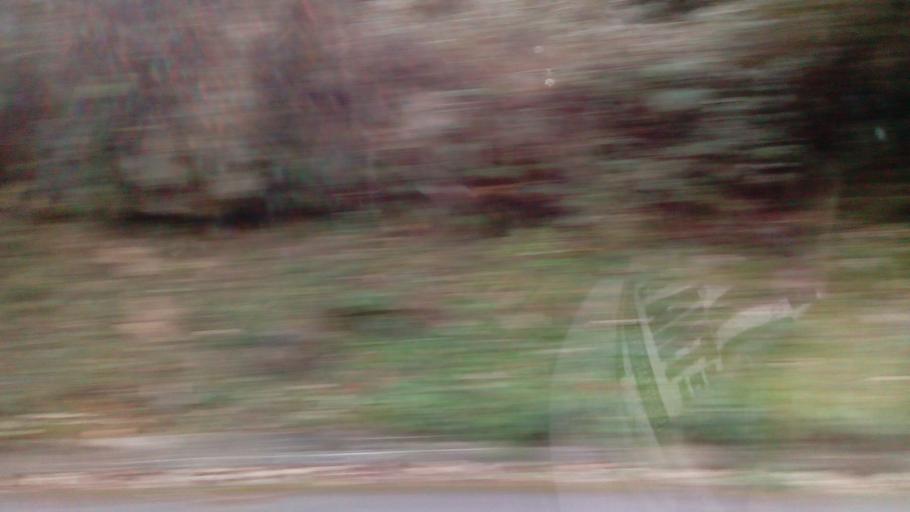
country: TW
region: Taiwan
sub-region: Hualien
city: Hualian
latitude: 24.3633
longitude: 121.3336
